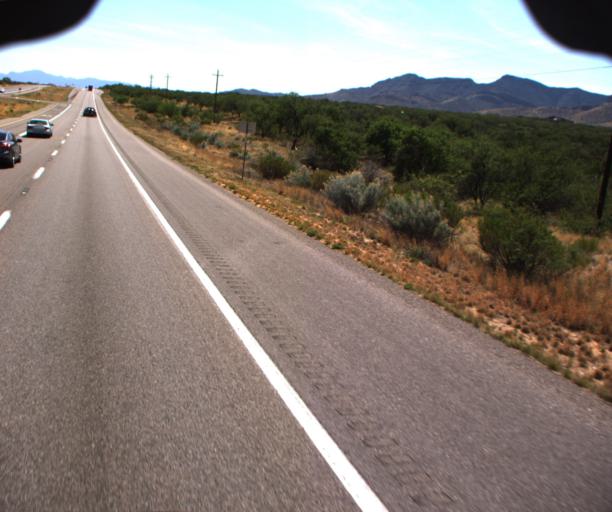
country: US
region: Arizona
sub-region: Cochise County
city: Whetstone
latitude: 31.8411
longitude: -110.3426
